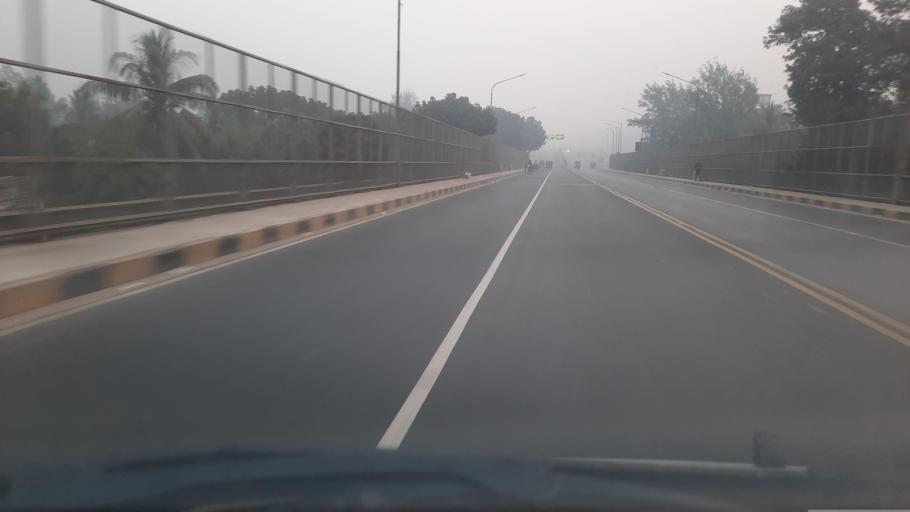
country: BD
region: Dhaka
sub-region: Dhaka
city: Dhaka
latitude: 23.6883
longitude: 90.4282
